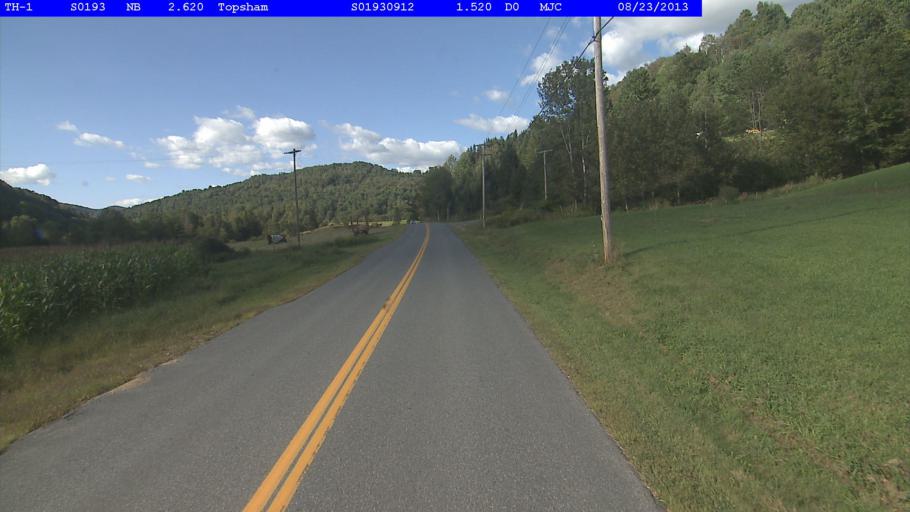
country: US
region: New Hampshire
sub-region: Grafton County
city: Haverhill
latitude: 44.0919
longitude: -72.2225
